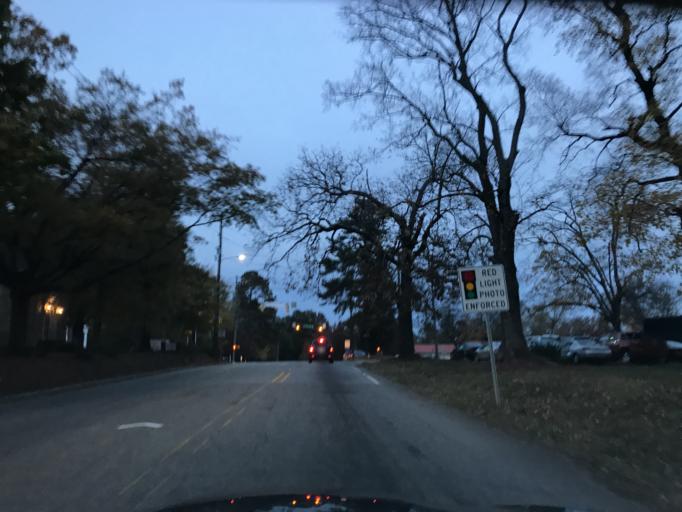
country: US
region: North Carolina
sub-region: Wake County
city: Raleigh
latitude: 35.8494
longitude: -78.6063
